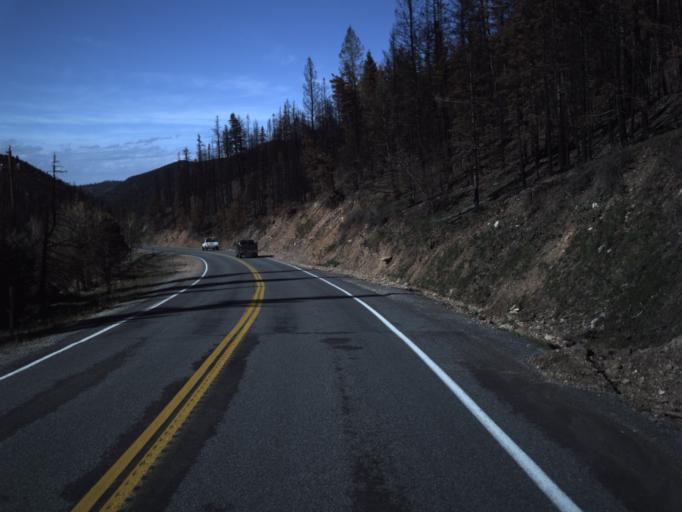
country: US
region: Utah
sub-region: Iron County
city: Parowan
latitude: 37.7360
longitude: -112.8376
